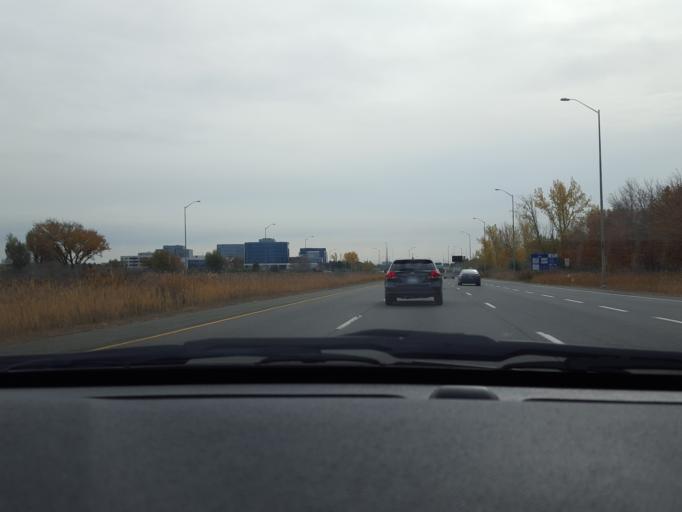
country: CA
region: Ontario
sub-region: York
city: Richmond Hill
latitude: 43.8615
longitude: -79.3748
